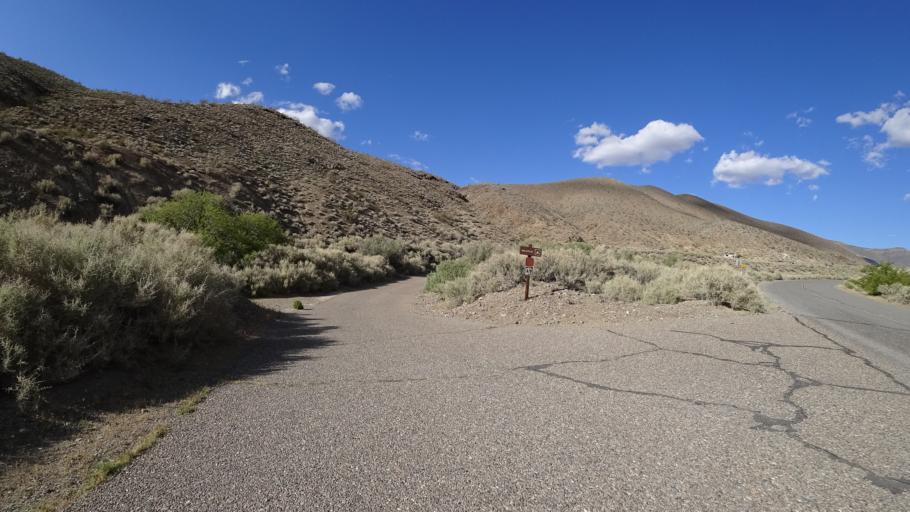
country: US
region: California
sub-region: San Bernardino County
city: Searles Valley
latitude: 36.2656
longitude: -117.1906
